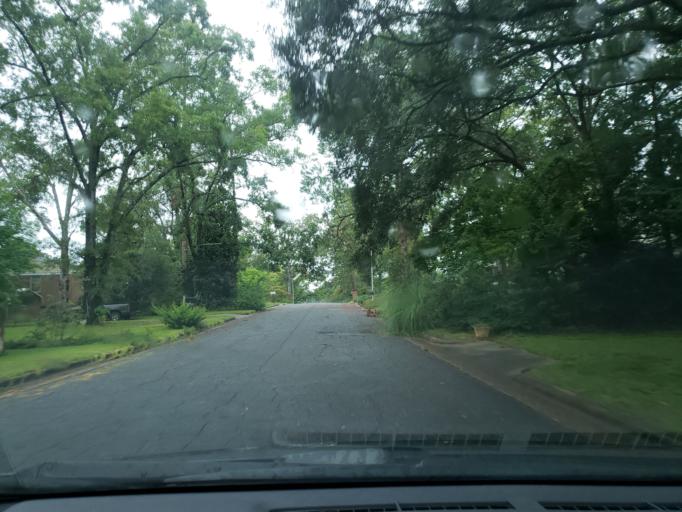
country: US
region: Georgia
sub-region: Dougherty County
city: Albany
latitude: 31.6062
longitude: -84.1854
